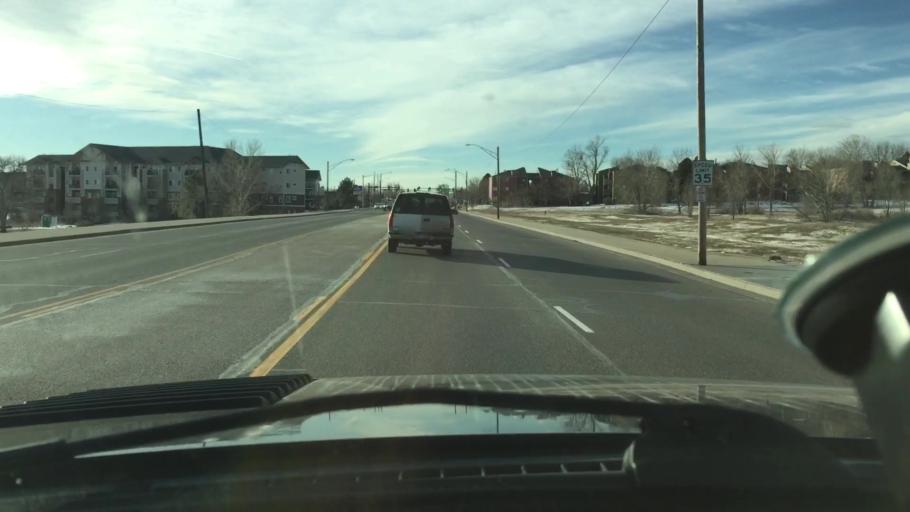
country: US
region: Colorado
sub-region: Adams County
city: Federal Heights
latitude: 39.8544
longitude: -105.0061
